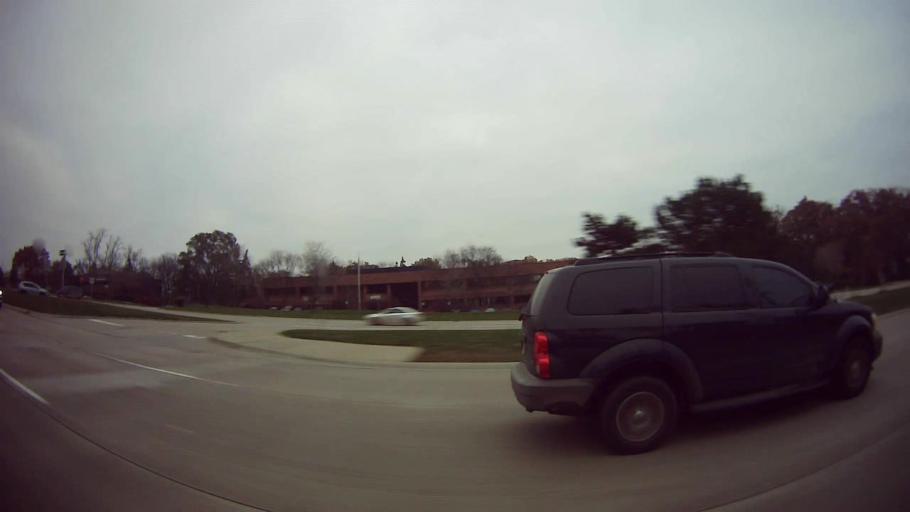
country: US
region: Michigan
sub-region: Oakland County
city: Bingham Farms
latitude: 42.5383
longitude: -83.2851
